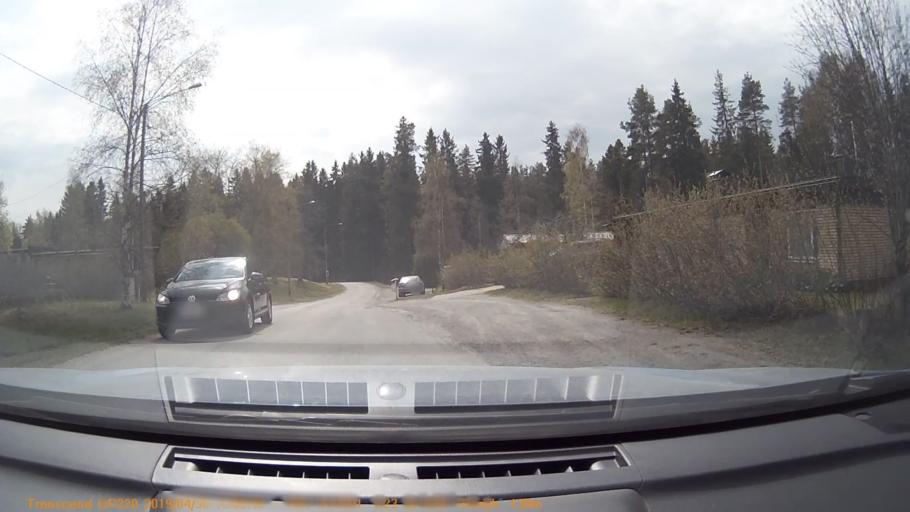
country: FI
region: Pirkanmaa
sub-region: Tampere
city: Yloejaervi
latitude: 61.5682
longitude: 23.6071
